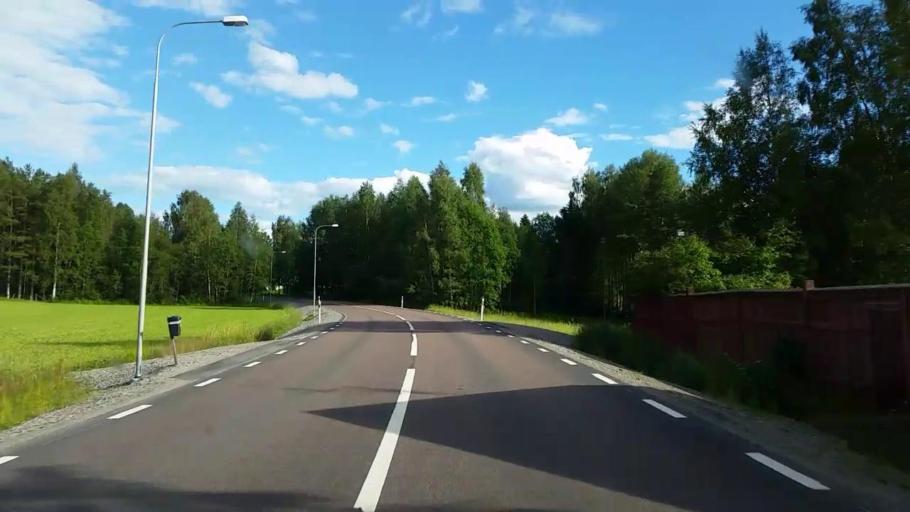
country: SE
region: Gaevleborg
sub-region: Ljusdals Kommun
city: Ljusdal
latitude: 61.8389
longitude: 16.0022
